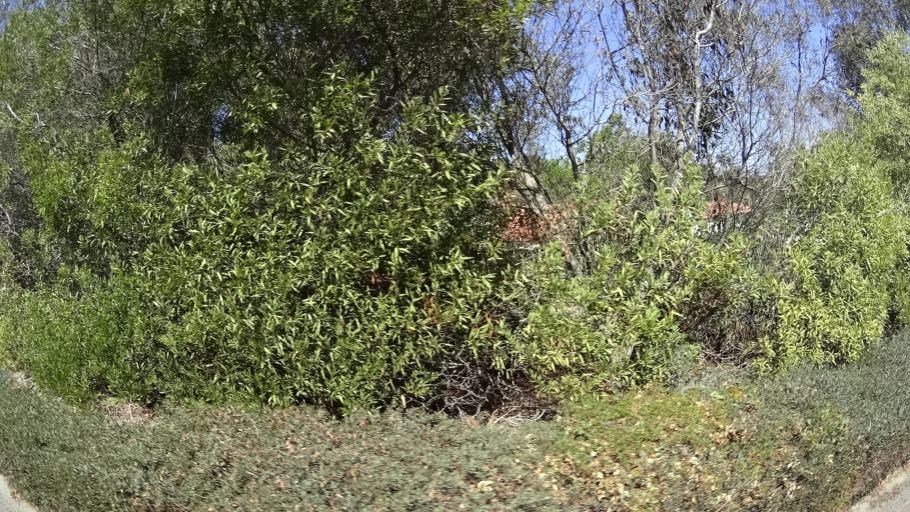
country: US
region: California
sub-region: San Diego County
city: Rancho Santa Fe
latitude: 33.0064
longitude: -117.2167
